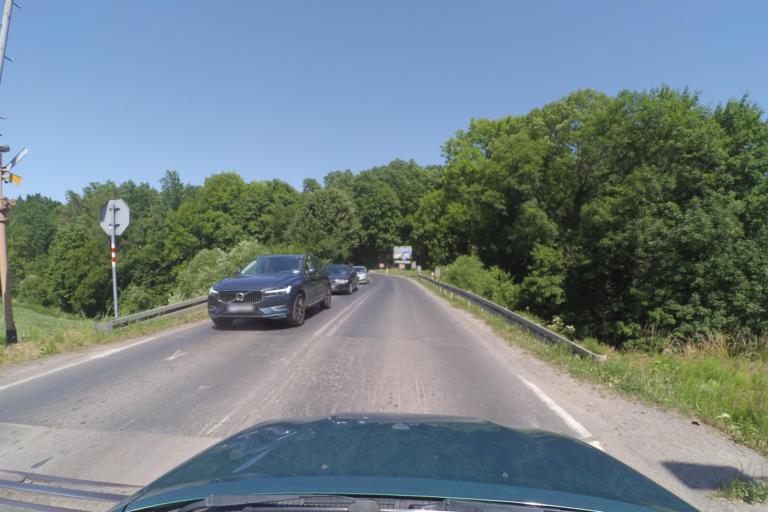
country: PL
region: Lower Silesian Voivodeship
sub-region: Powiat zlotoryjski
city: Zlotoryja
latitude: 51.1070
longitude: 15.9000
